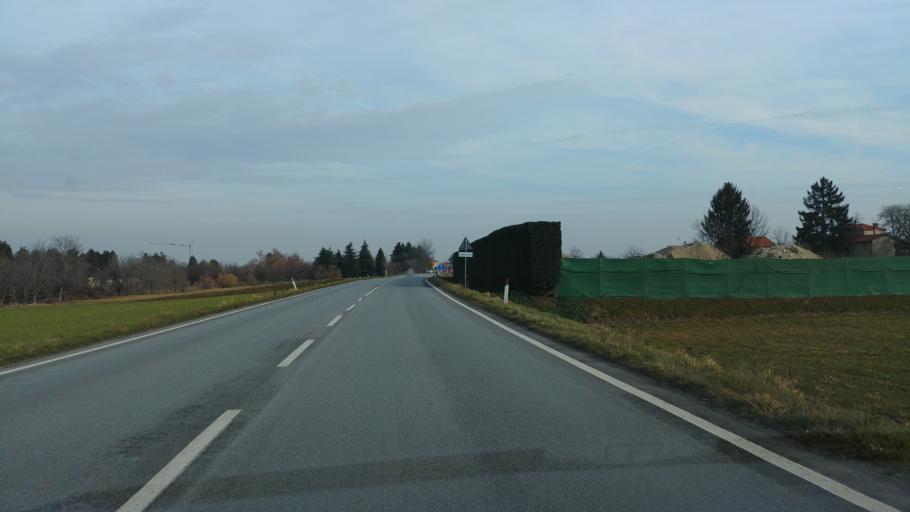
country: IT
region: Piedmont
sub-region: Provincia di Cuneo
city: Cuneo
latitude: 44.3753
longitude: 7.5549
